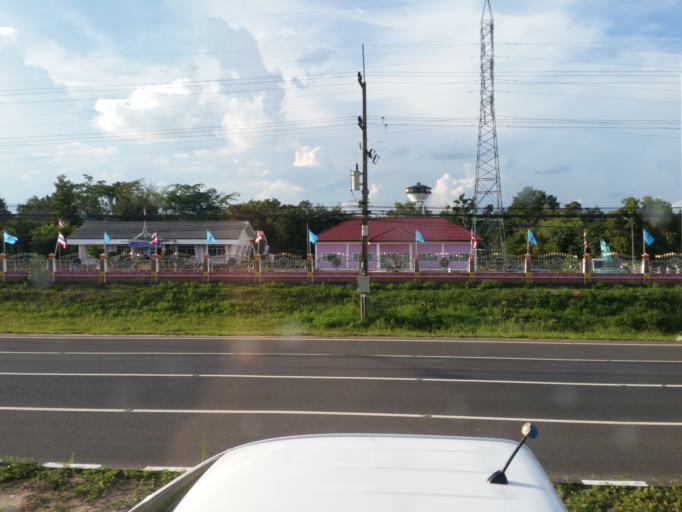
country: TH
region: Changwat Ubon Ratchathani
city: Sirindhorn
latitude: 15.2007
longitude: 105.3893
